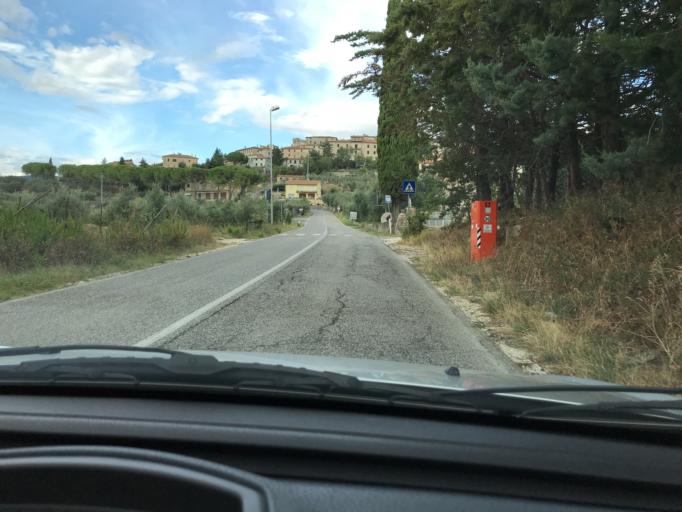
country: IT
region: Umbria
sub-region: Provincia di Terni
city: Montecchio
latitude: 42.6604
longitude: 12.2821
